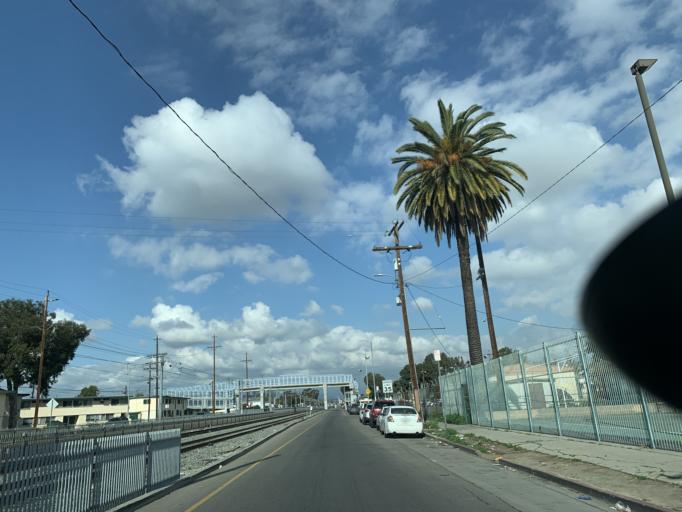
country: US
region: California
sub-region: Los Angeles County
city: Huntington Park
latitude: 33.9931
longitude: -118.2431
